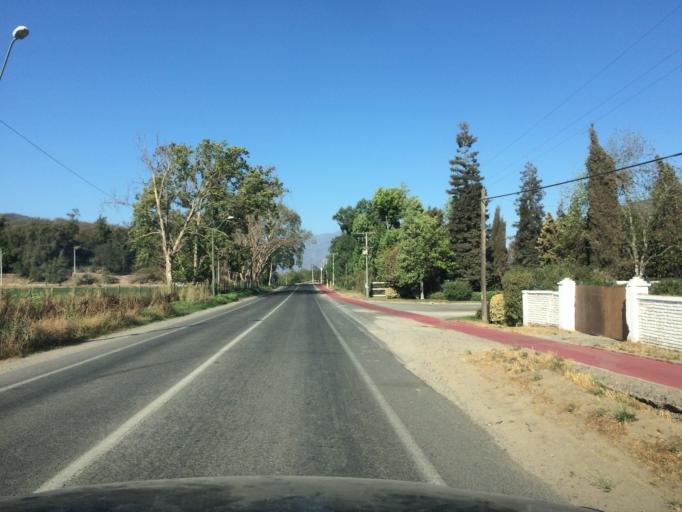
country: CL
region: Santiago Metropolitan
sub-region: Provincia de Melipilla
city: Melipilla
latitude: -33.4908
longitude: -71.1492
